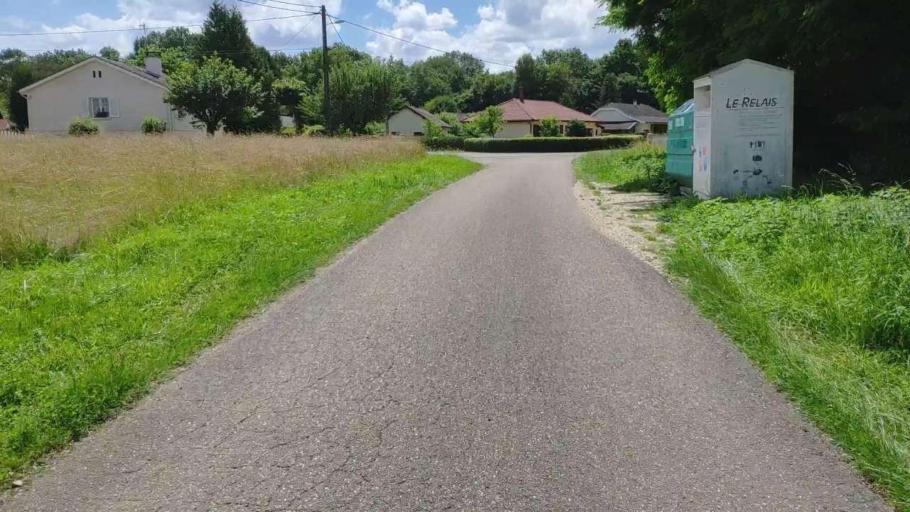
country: FR
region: Franche-Comte
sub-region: Departement du Jura
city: Bletterans
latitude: 46.8428
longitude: 5.4721
